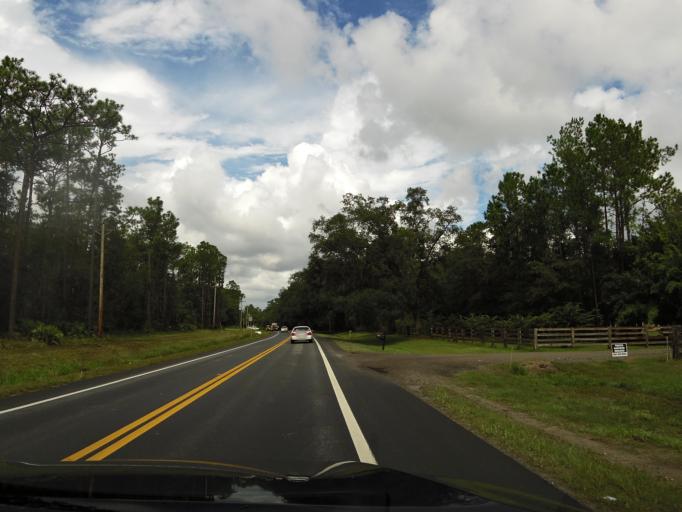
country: US
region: Florida
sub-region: Clay County
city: Middleburg
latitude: 30.1271
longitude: -81.9989
